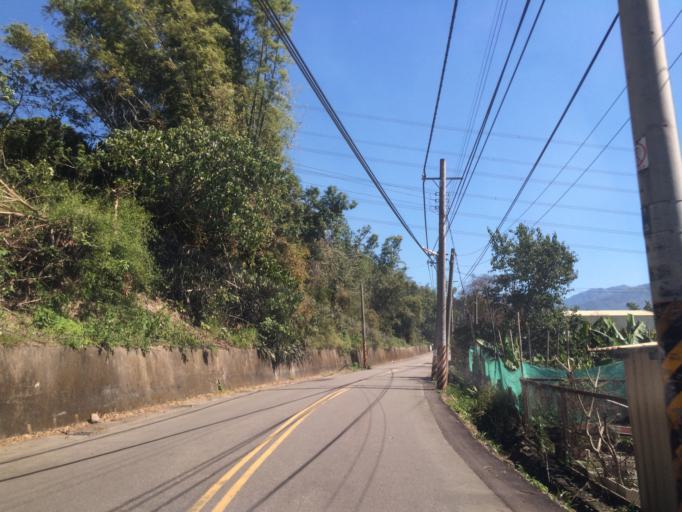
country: TW
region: Taiwan
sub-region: Yunlin
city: Douliu
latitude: 23.7013
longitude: 120.6110
